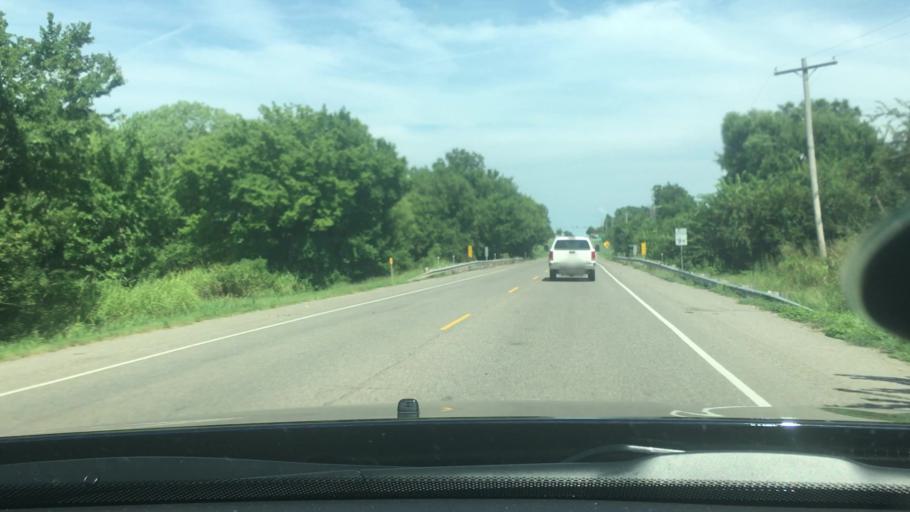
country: US
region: Oklahoma
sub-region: Pottawatomie County
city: Shawnee
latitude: 35.3331
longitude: -96.8130
